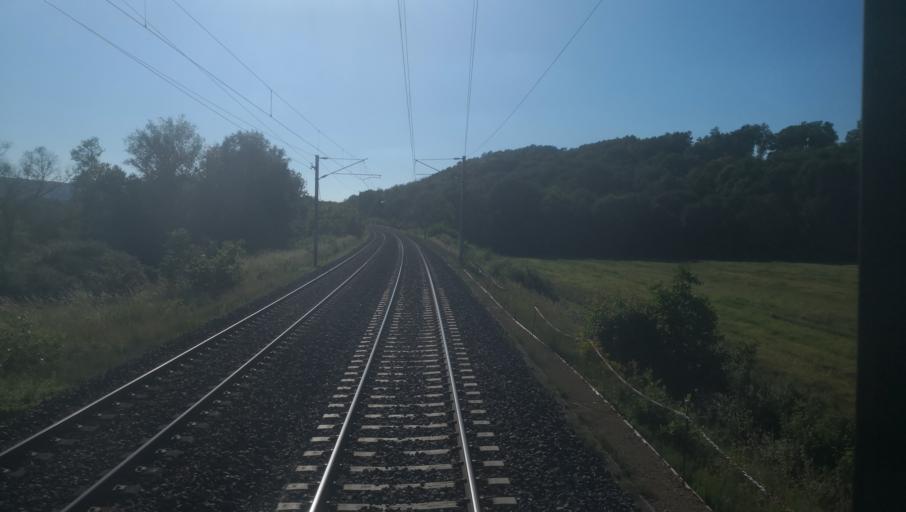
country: FR
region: Bourgogne
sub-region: Departement de la Nievre
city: Pouilly-sur-Loire
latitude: 47.3169
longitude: 2.9013
